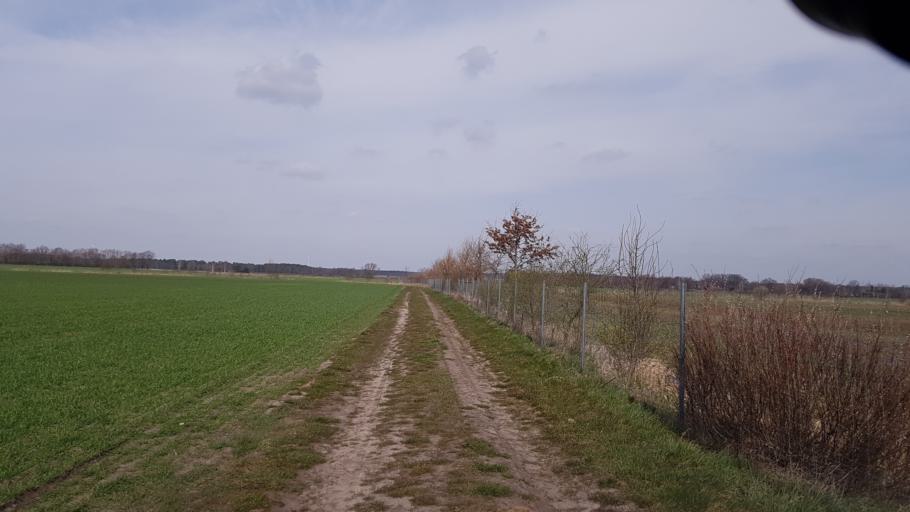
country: DE
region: Brandenburg
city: Bronkow
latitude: 51.6361
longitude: 13.9199
